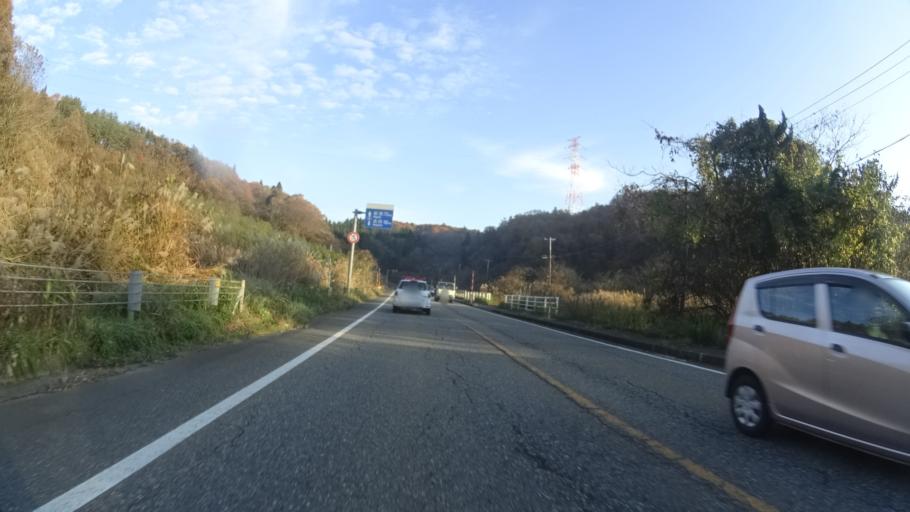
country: JP
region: Niigata
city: Kashiwazaki
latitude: 37.4062
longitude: 138.6881
